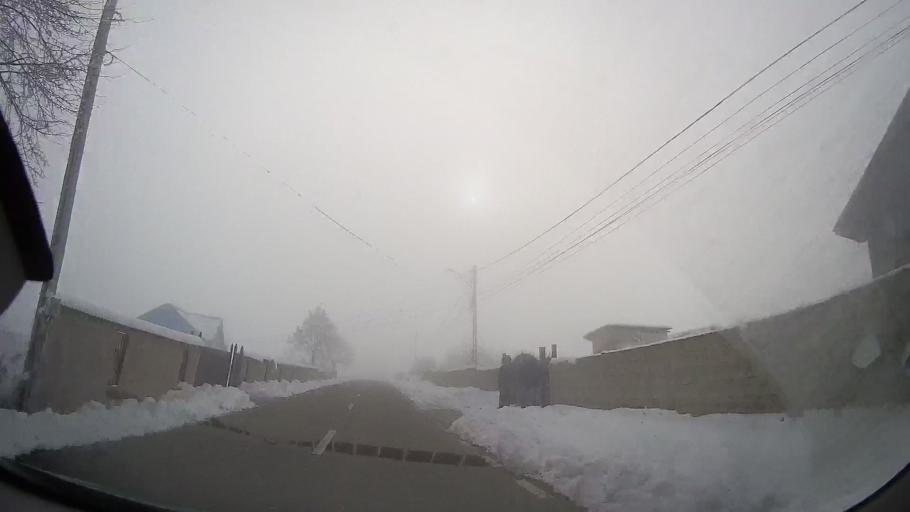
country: RO
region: Iasi
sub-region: Comuna Valea Seaca
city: Valea Seaca
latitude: 47.2819
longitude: 26.6699
